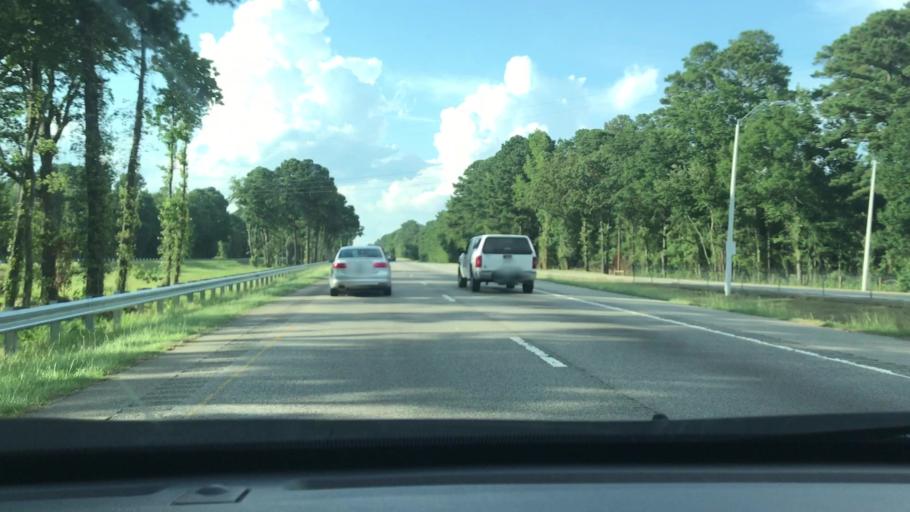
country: US
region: North Carolina
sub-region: Robeson County
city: Lumberton
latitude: 34.7072
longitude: -78.9976
